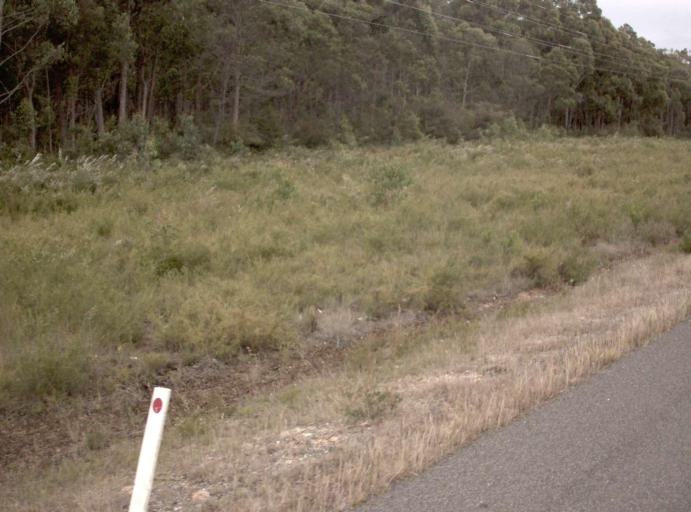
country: AU
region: Victoria
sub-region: East Gippsland
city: Lakes Entrance
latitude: -37.7244
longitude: 147.9539
